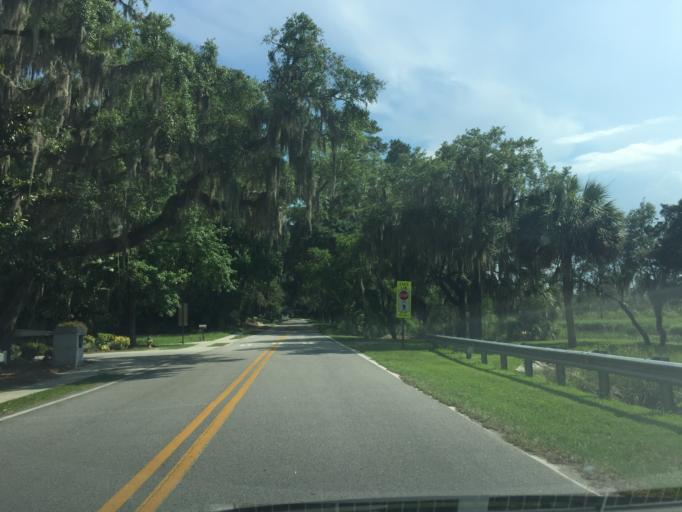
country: US
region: Georgia
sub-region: Chatham County
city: Isle of Hope
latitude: 31.9899
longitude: -81.1026
